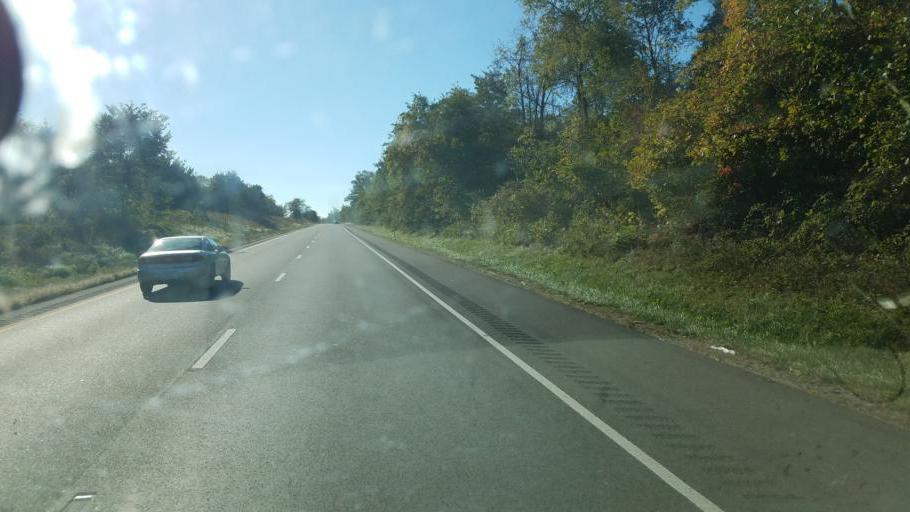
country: US
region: Maryland
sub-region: Washington County
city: Hancock
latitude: 39.6508
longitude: -78.0455
